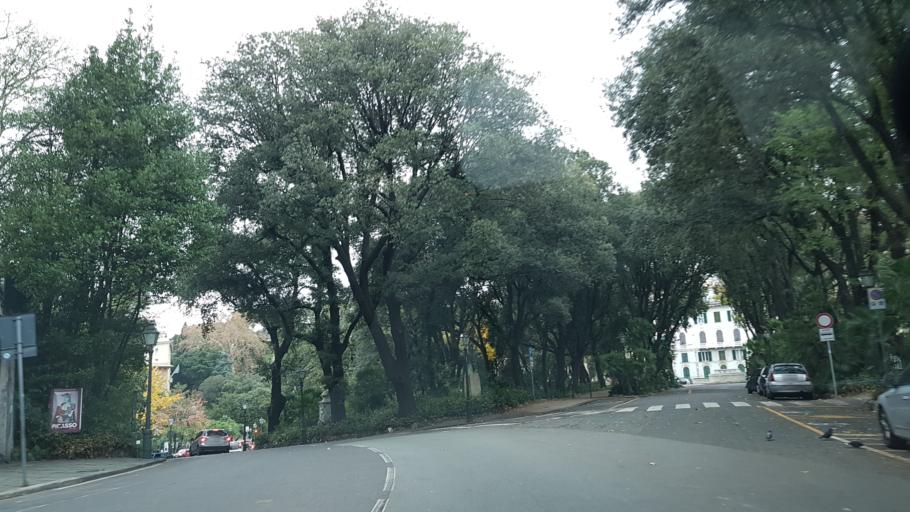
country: IT
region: Liguria
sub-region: Provincia di Genova
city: Genoa
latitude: 44.4087
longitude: 8.9396
